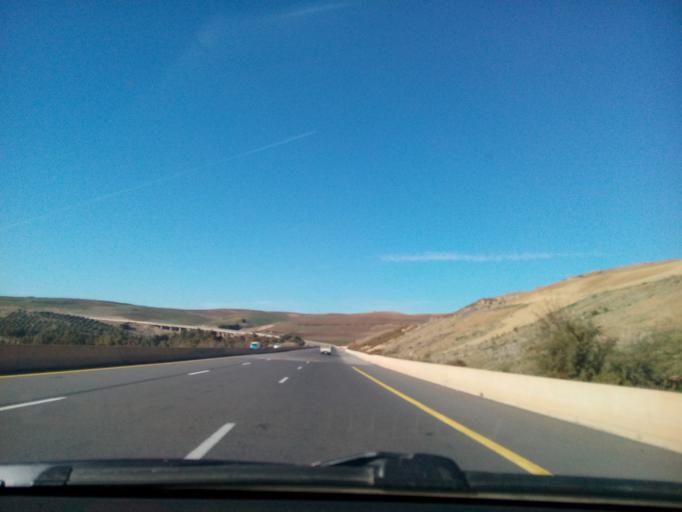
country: DZ
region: Tlemcen
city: Sidi Abdelli
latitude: 35.0382
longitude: -1.0554
